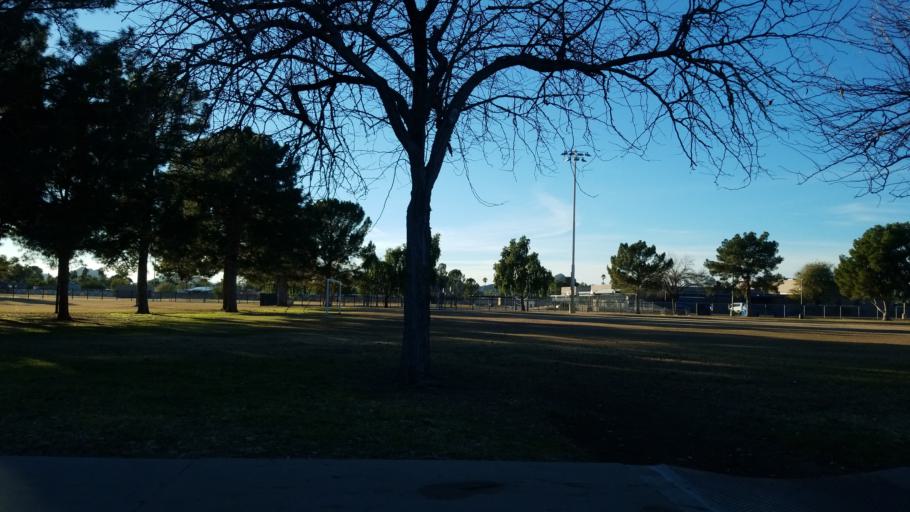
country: US
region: Arizona
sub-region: Maricopa County
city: Paradise Valley
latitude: 33.6060
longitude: -111.9880
